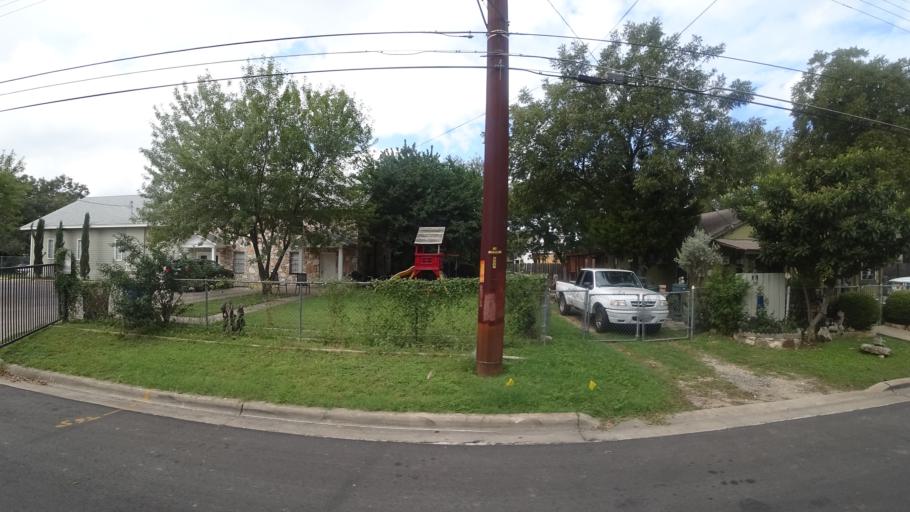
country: US
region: Texas
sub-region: Travis County
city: Austin
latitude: 30.2549
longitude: -97.7108
